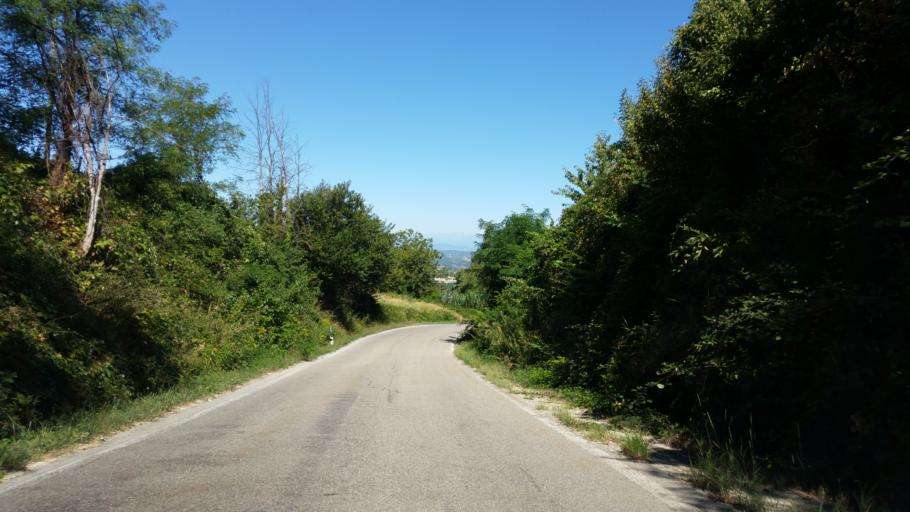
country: IT
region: Piedmont
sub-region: Provincia di Cuneo
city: Neviglie
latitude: 44.6862
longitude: 8.1255
